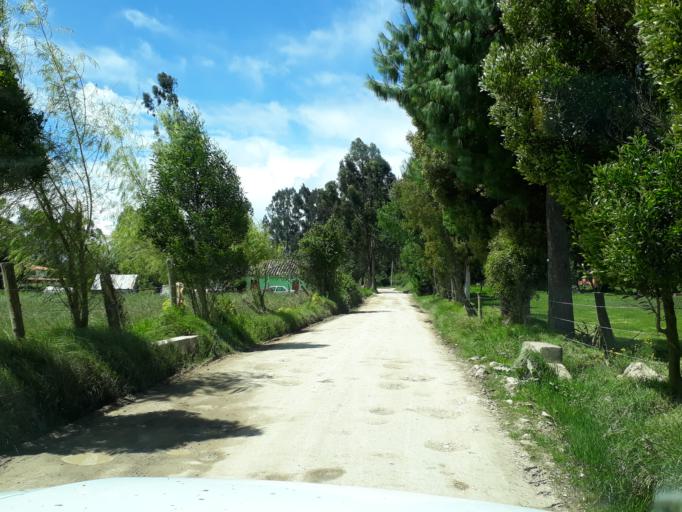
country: CO
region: Cundinamarca
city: Guasca
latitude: 4.8503
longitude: -73.8819
